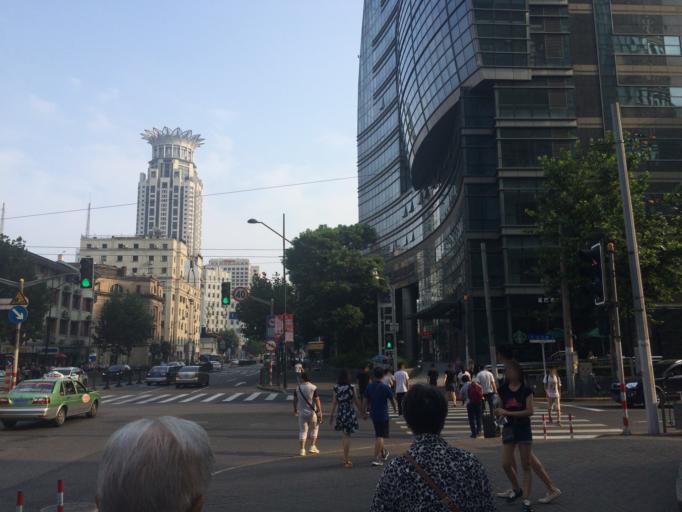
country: CN
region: Shanghai Shi
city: Hongkou
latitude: 31.2389
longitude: 121.4806
